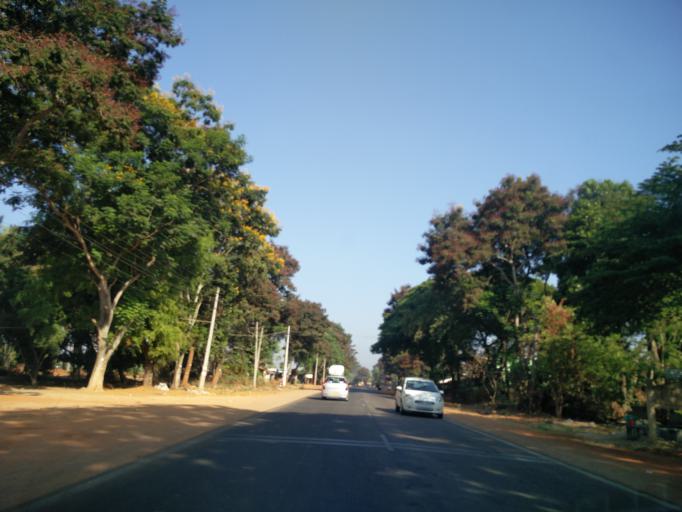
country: IN
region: Karnataka
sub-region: Tumkur
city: Gubbi
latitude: 13.3105
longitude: 76.9199
